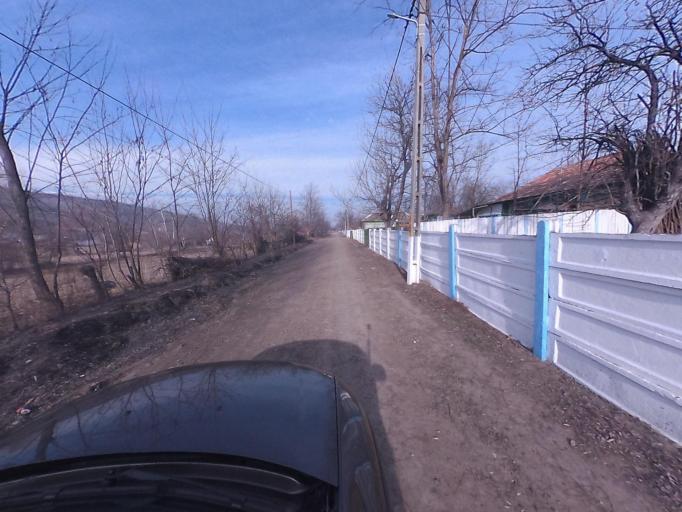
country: RO
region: Vaslui
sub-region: Comuna Solesti
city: Solesti
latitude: 46.8061
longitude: 27.7815
